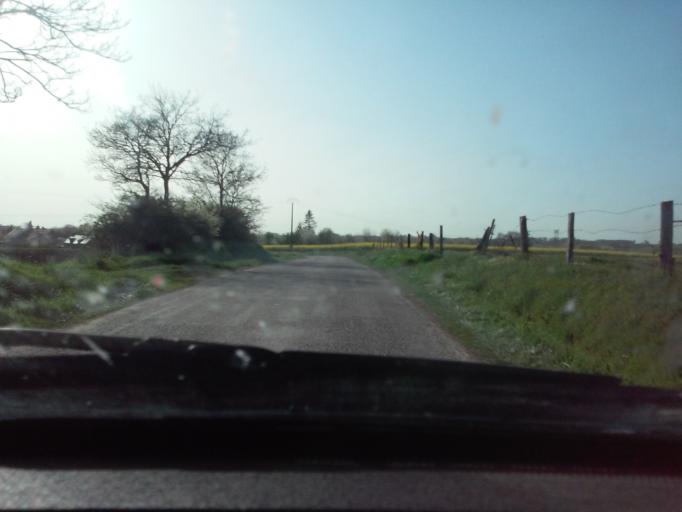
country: FR
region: Brittany
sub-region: Departement d'Ille-et-Vilaine
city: Romagne
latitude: 48.3013
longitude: -1.2790
